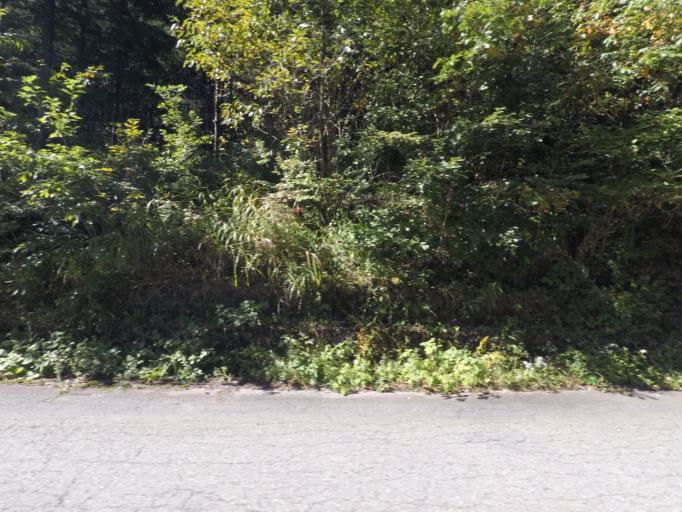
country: JP
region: Nagano
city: Tatsuno
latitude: 35.9732
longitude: 137.7428
